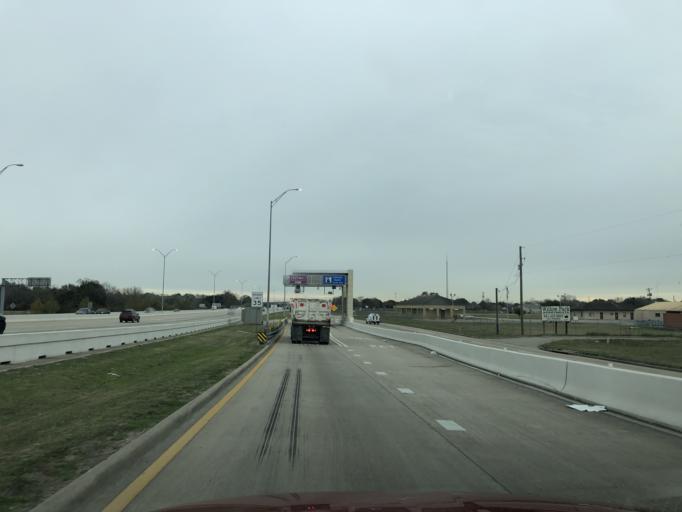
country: US
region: Texas
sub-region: Fort Bend County
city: Missouri City
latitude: 29.6193
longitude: -95.5059
